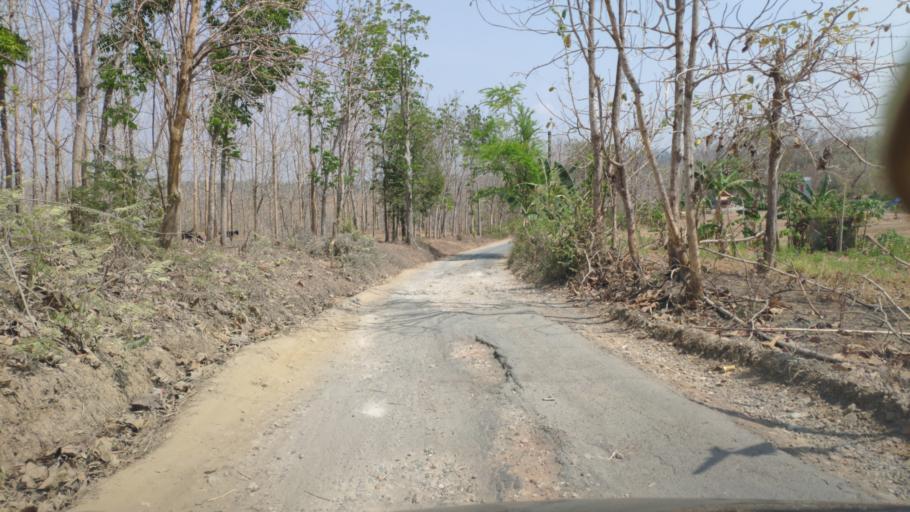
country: ID
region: Central Java
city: Gaplokan
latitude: -6.8989
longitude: 111.2684
